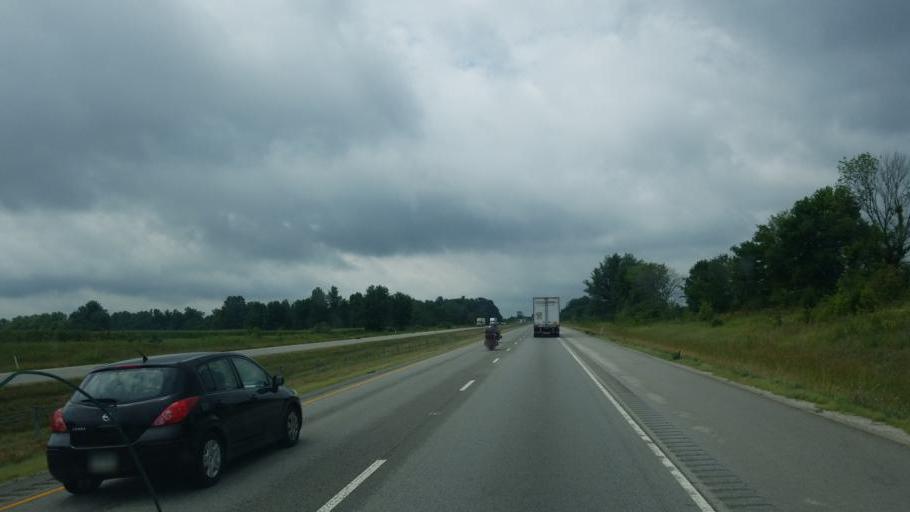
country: US
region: Indiana
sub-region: Clay County
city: Brazil
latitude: 39.4772
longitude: -87.0172
